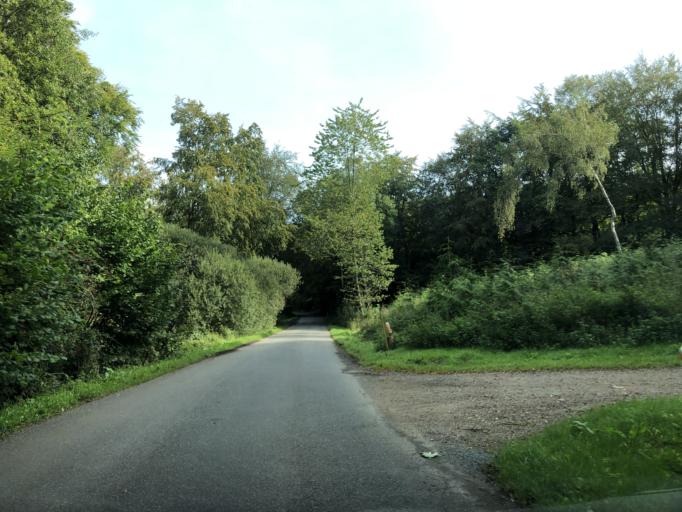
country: DK
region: South Denmark
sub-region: Vejle Kommune
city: Borkop
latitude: 55.6074
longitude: 9.6677
